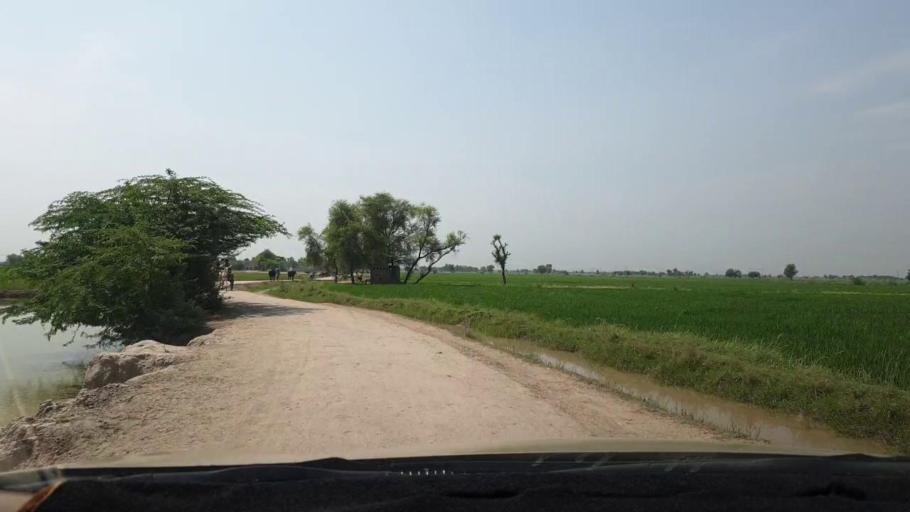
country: PK
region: Sindh
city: Naudero
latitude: 27.6525
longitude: 68.2594
